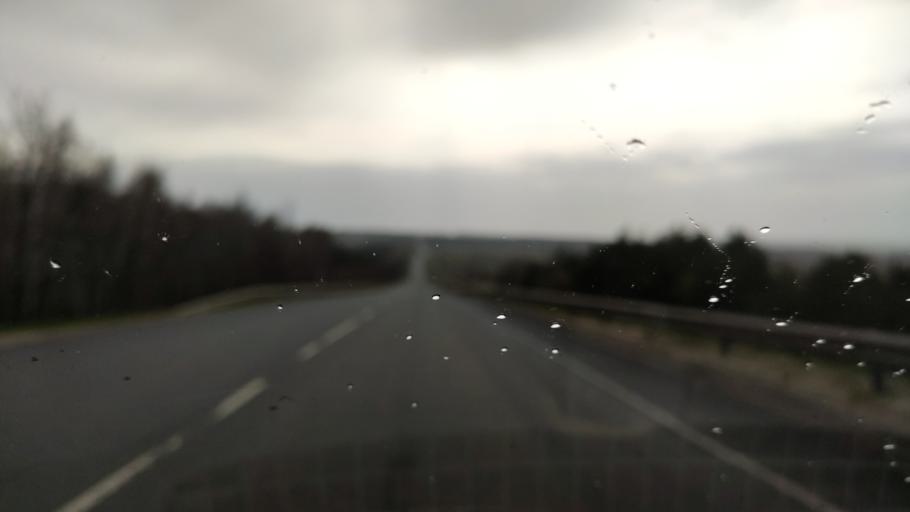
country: RU
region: Kursk
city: Gorshechnoye
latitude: 51.4799
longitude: 37.9555
